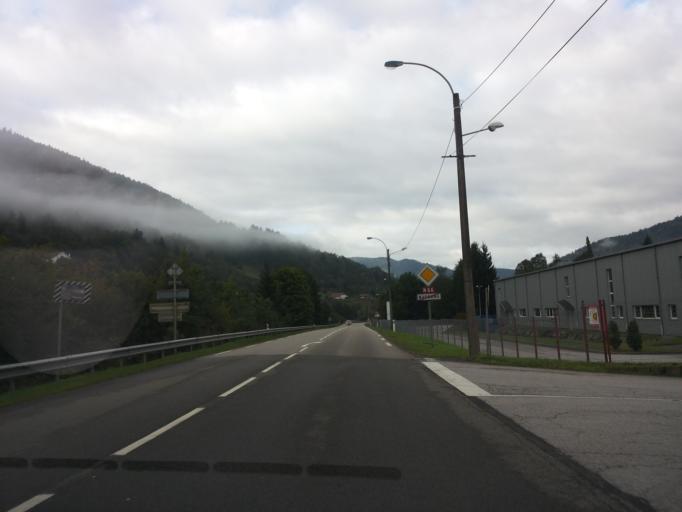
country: FR
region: Lorraine
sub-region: Departement des Vosges
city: Bussang
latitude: 47.8789
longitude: 6.8494
